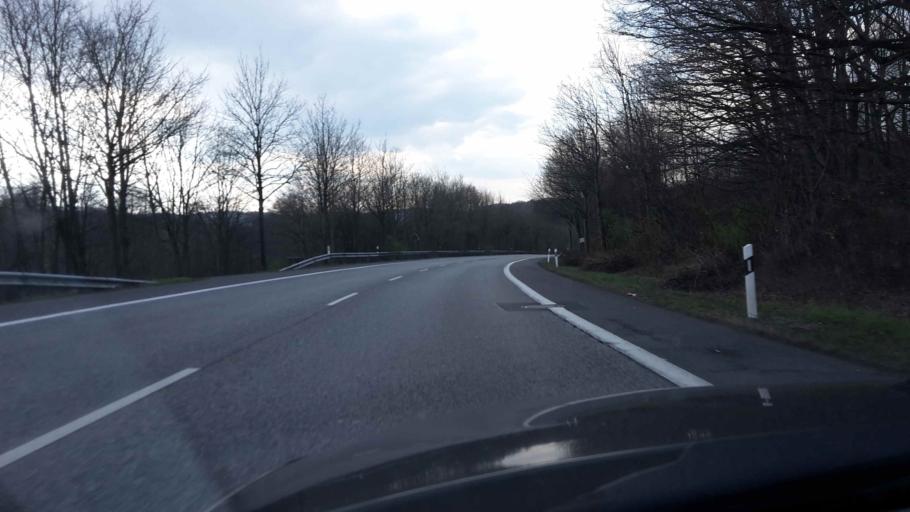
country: DE
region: North Rhine-Westphalia
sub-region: Regierungsbezirk Koln
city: Hennef
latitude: 50.7060
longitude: 7.3055
